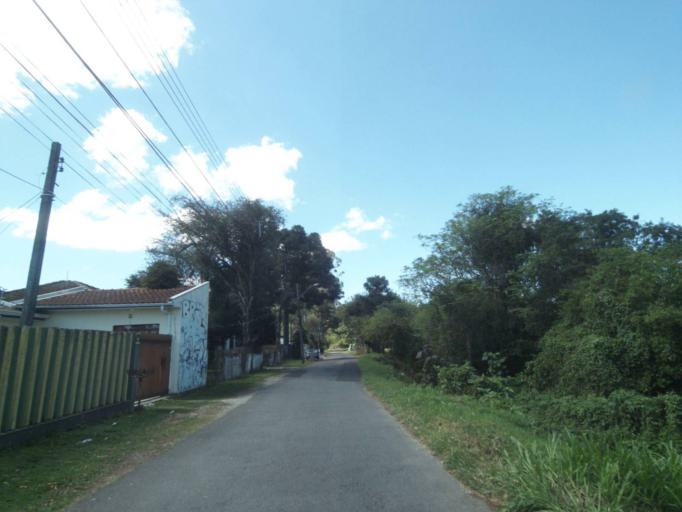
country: BR
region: Parana
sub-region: Curitiba
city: Curitiba
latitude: -25.3869
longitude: -49.2409
